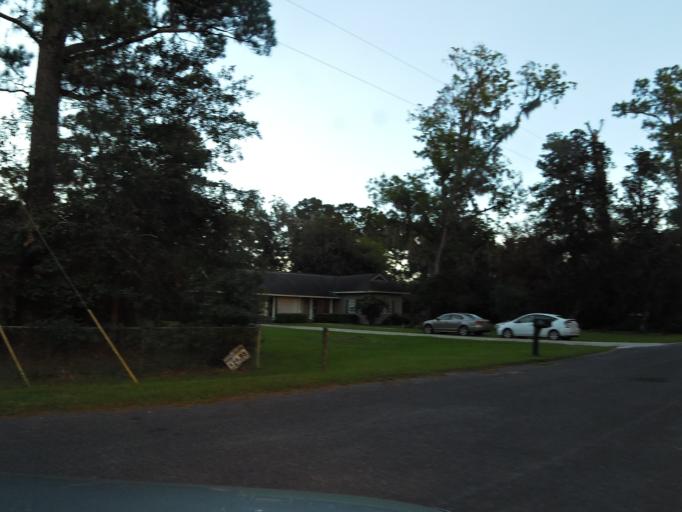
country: US
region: Georgia
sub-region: Camden County
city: Kingsland
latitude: 30.7740
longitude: -81.7086
